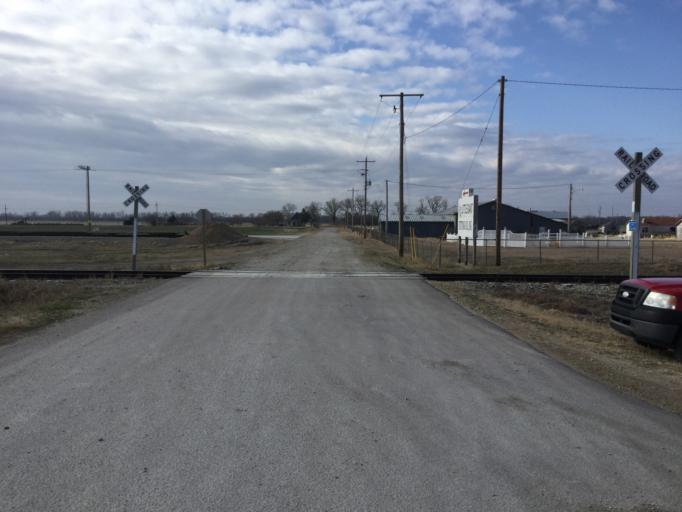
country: US
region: Kansas
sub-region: Barton County
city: Great Bend
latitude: 38.3647
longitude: -98.6824
